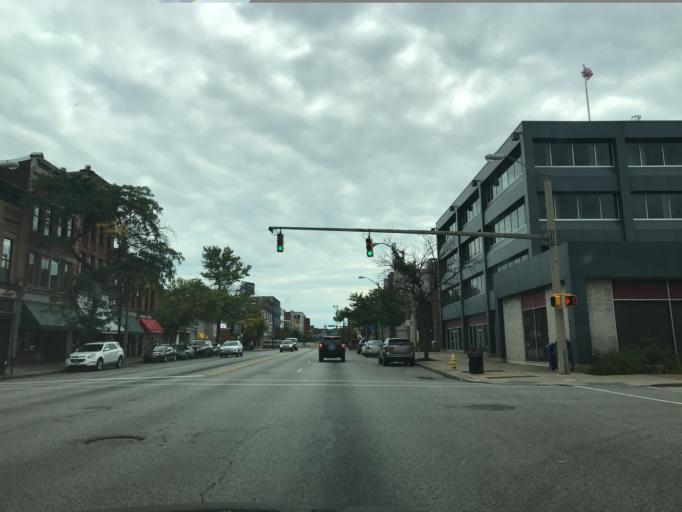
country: US
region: Pennsylvania
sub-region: Erie County
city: Erie
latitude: 42.1246
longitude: -80.0821
